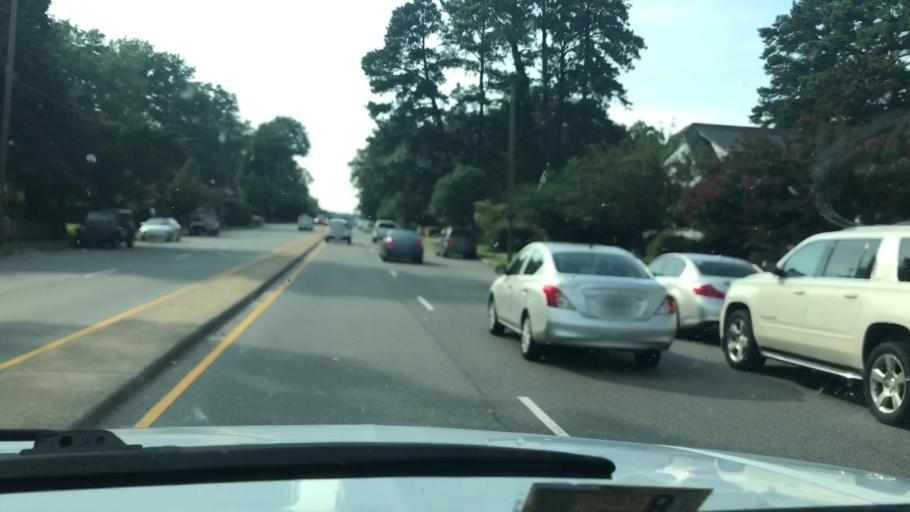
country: US
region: Virginia
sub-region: Henrico County
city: Dumbarton
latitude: 37.5733
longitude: -77.5035
